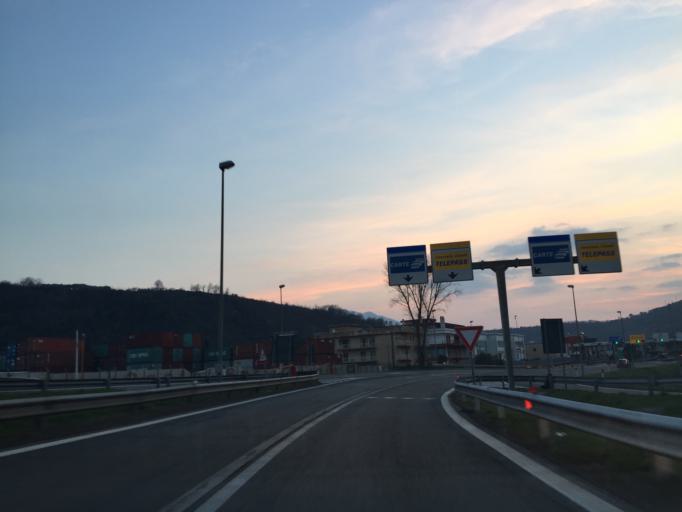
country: IT
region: Campania
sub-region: Provincia di Salerno
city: Casali-San Potito
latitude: 40.7702
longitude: 14.6661
